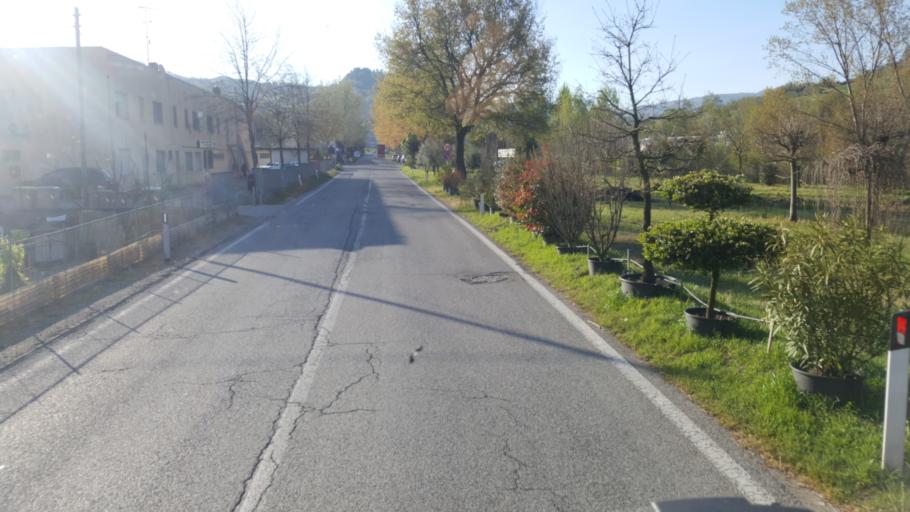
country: SM
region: Acquaviva
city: Acquaviva
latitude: 43.9415
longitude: 12.4071
